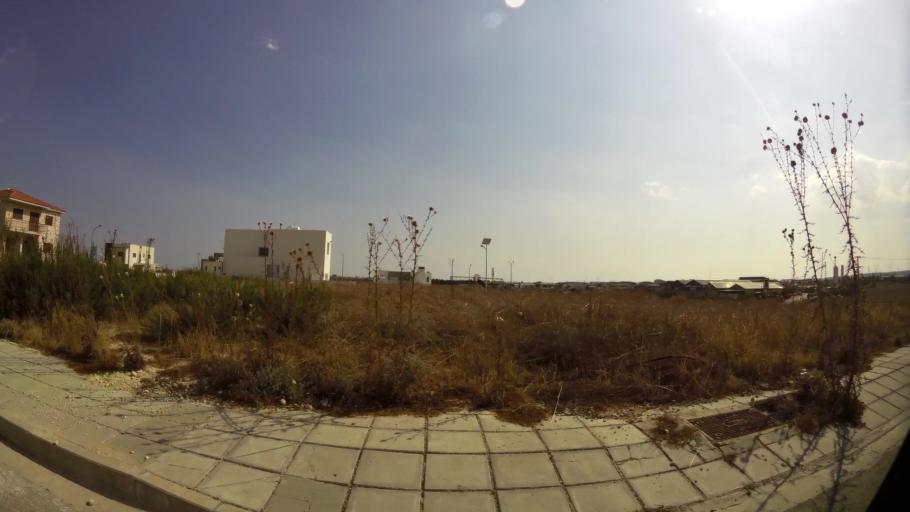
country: CY
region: Larnaka
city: Dhromolaxia
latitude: 34.9061
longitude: 33.5793
